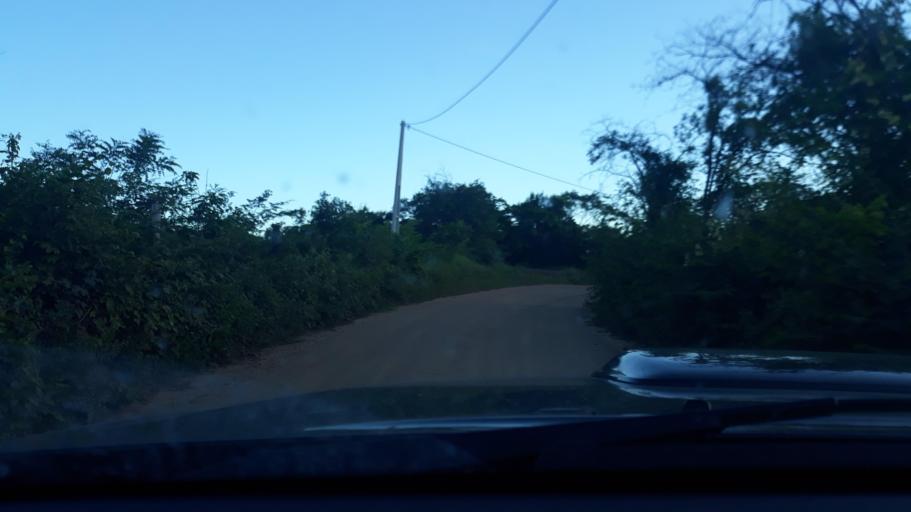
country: BR
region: Bahia
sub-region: Riacho De Santana
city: Riacho de Santana
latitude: -13.8040
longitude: -42.7123
